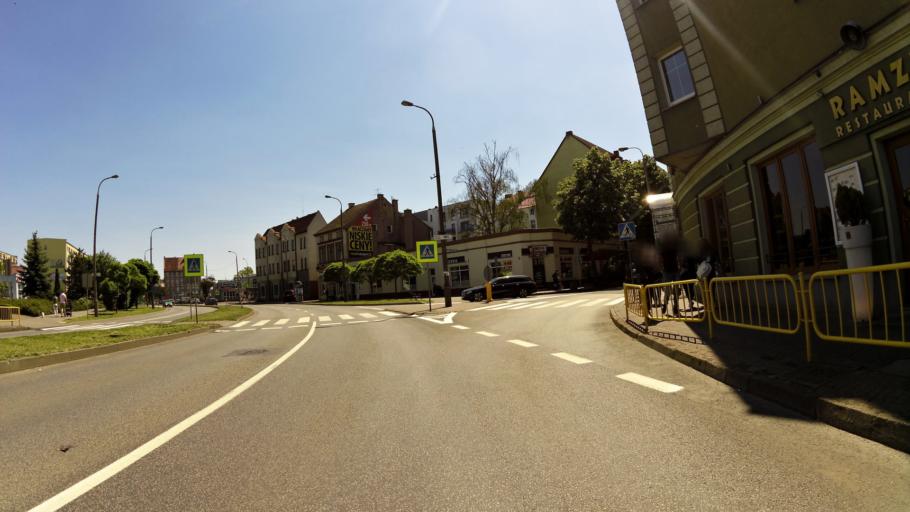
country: PL
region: Lubusz
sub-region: Powiat slubicki
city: Slubice
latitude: 52.3510
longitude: 14.5603
